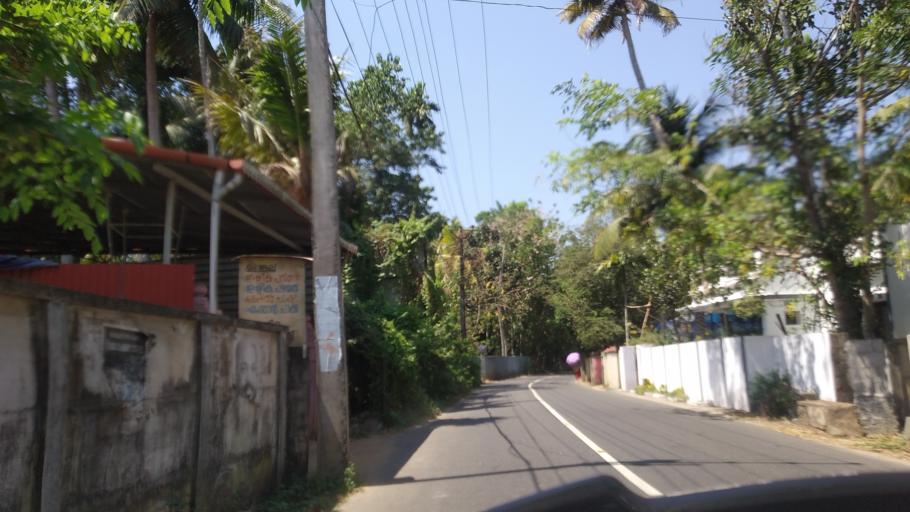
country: IN
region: Kerala
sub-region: Thrissur District
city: Kodungallur
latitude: 10.1778
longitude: 76.2125
